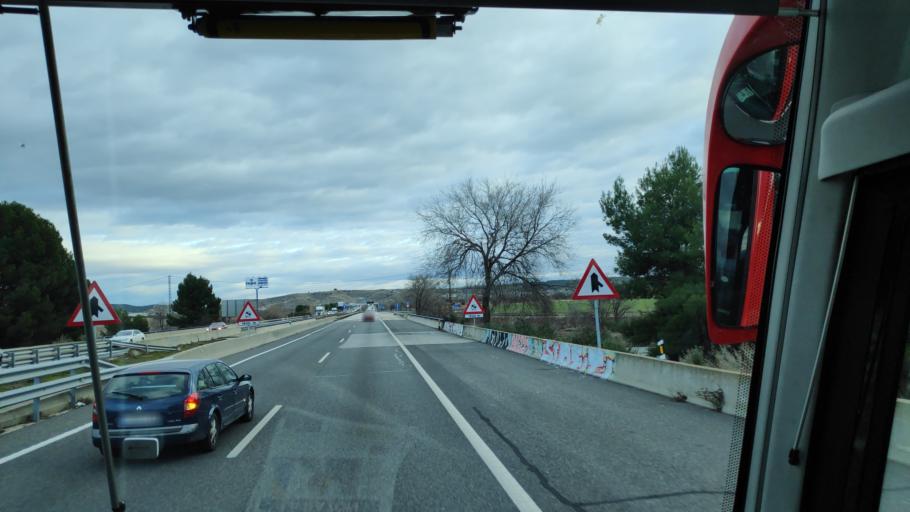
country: ES
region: Madrid
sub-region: Provincia de Madrid
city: Vaciamadrid
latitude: 40.3100
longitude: -3.4927
